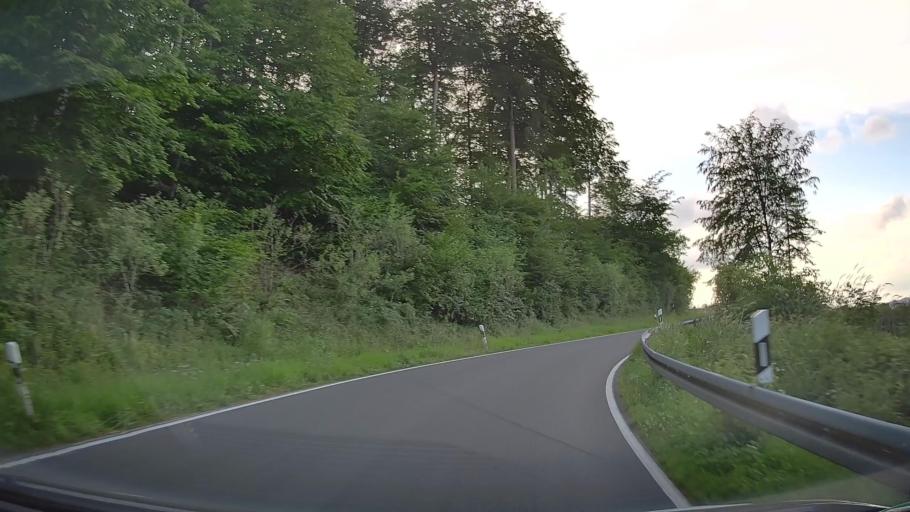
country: DE
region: North Rhine-Westphalia
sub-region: Regierungsbezirk Detmold
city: Barntrup
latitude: 51.9679
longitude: 9.1551
